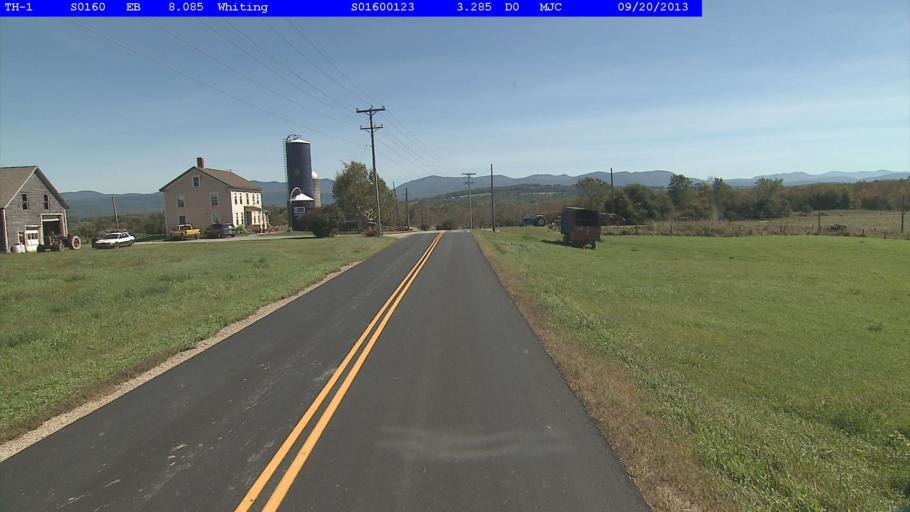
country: US
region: Vermont
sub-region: Rutland County
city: Brandon
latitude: 43.8518
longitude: -73.1651
